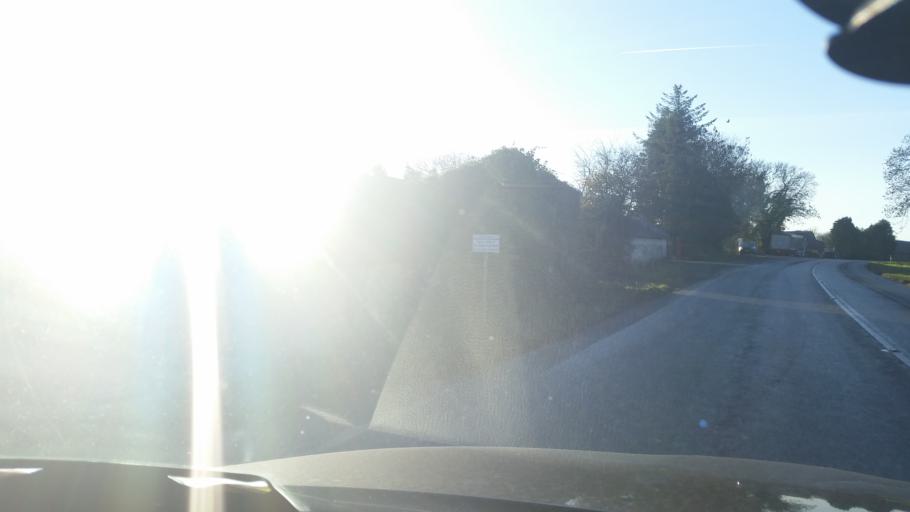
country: IE
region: Leinster
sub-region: Loch Garman
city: Gorey
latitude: 52.5770
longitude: -6.3147
